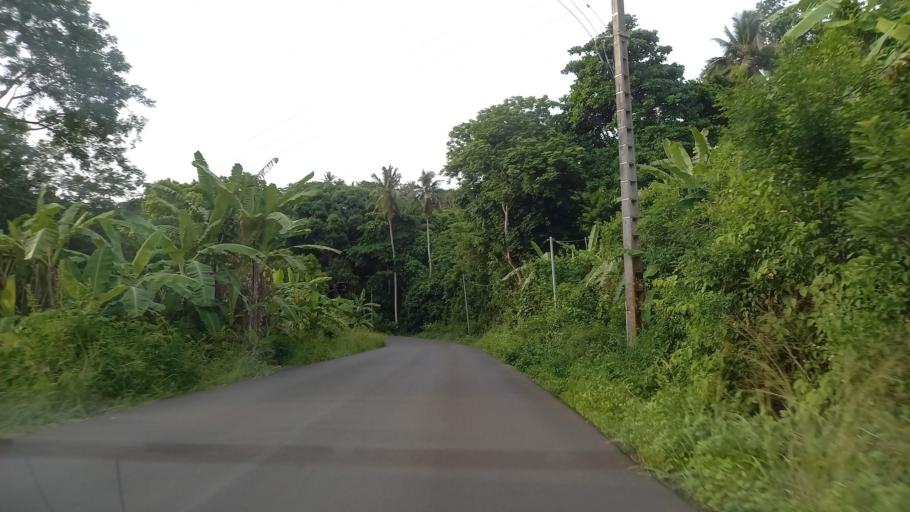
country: YT
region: Acoua
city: Acoua
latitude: -12.7478
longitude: 45.0594
